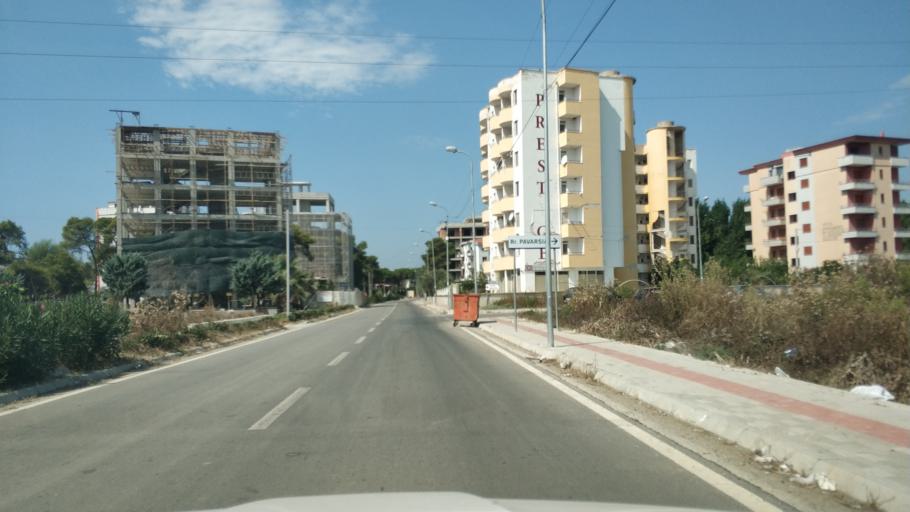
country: AL
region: Tirane
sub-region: Rrethi i Kavajes
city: Golem
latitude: 41.2369
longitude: 19.5223
